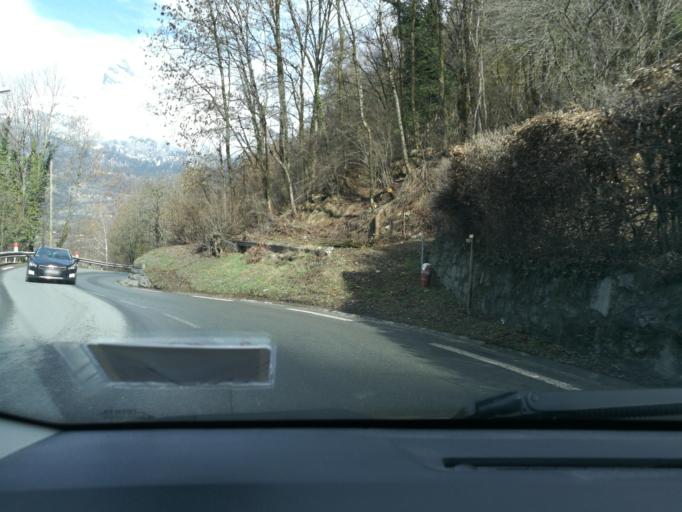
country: FR
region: Rhone-Alpes
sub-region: Departement de la Haute-Savoie
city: Saint-Gervais-les-Bains
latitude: 45.9031
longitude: 6.7136
